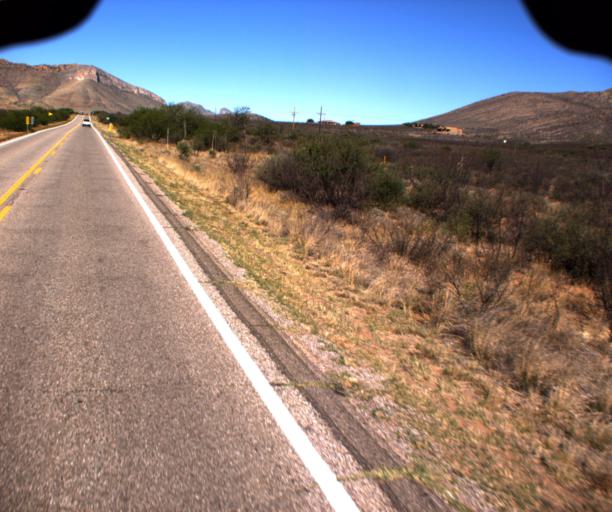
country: US
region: Arizona
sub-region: Cochise County
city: Huachuca City
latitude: 31.6919
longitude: -110.3886
